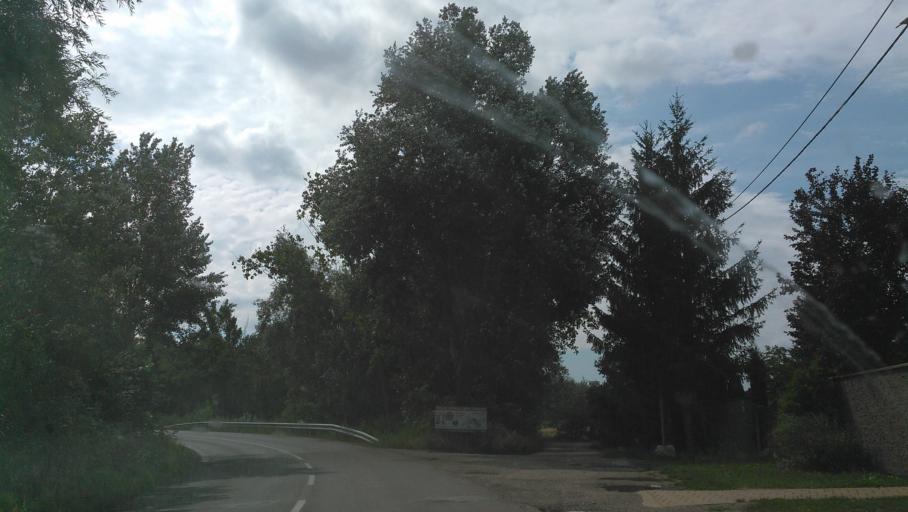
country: SK
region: Bratislavsky
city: Dunajska Luzna
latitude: 48.1554
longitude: 17.2828
